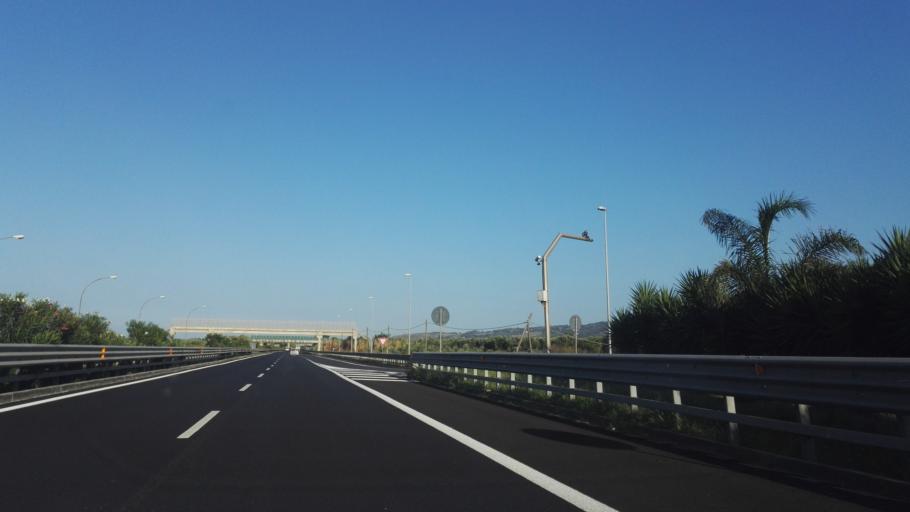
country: IT
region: Calabria
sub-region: Provincia di Catanzaro
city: Santa Eufemia Lamezia
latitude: 38.9299
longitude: 16.2359
